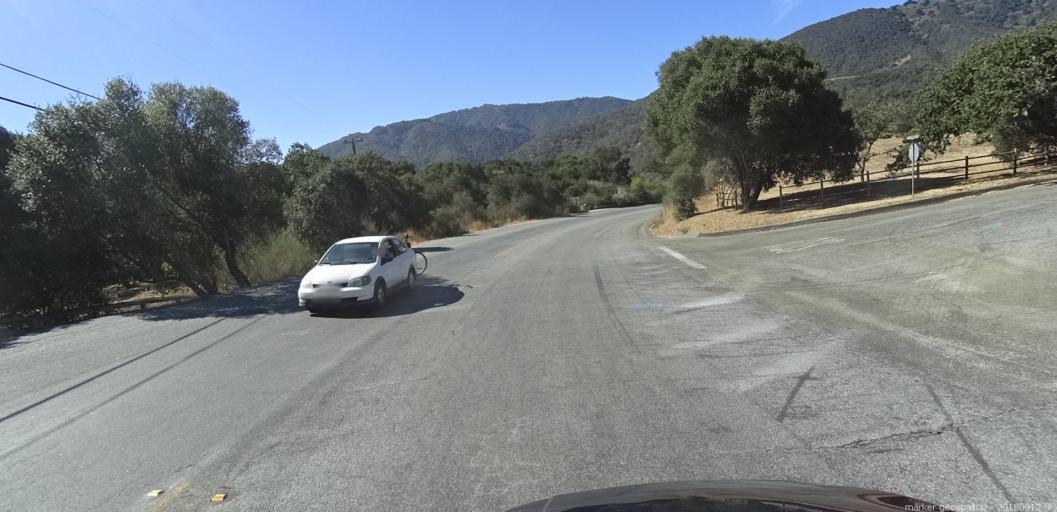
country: US
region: California
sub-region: Monterey County
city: Carmel Valley Village
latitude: 36.5036
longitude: -121.7522
